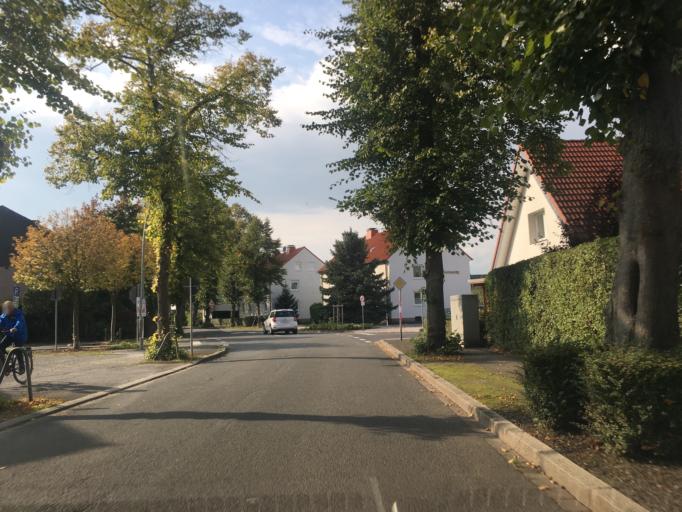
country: DE
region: North Rhine-Westphalia
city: Selm
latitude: 51.7032
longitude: 7.4686
